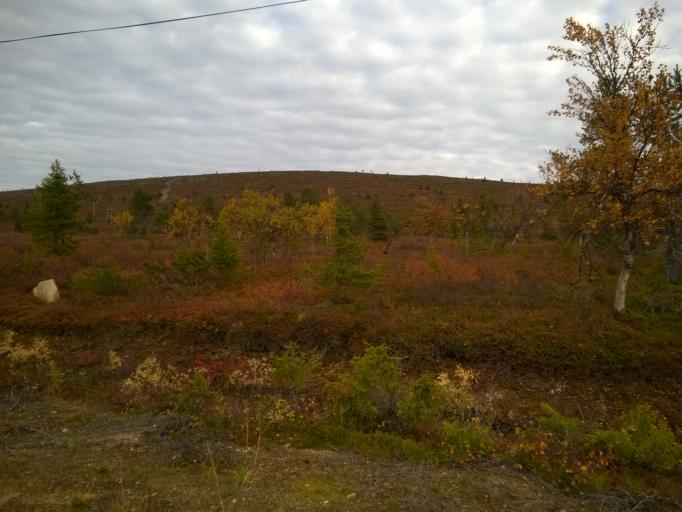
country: FI
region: Lapland
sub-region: Tunturi-Lappi
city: Muonio
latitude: 67.9715
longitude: 24.0972
